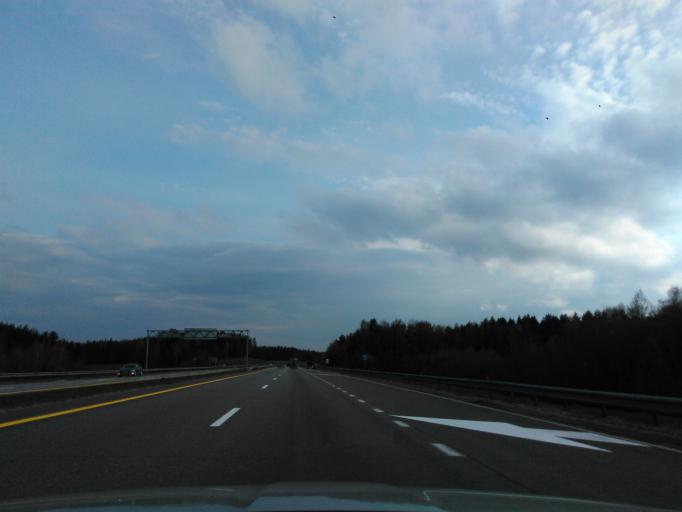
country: BY
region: Minsk
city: Astrashytski Haradok
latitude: 54.0512
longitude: 27.7026
